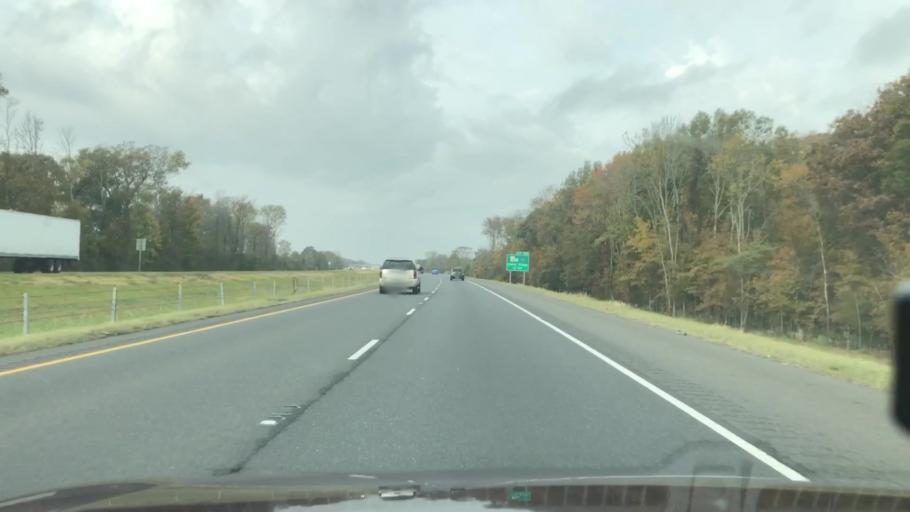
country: US
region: Louisiana
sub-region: Richland Parish
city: Delhi
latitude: 32.4559
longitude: -91.6132
